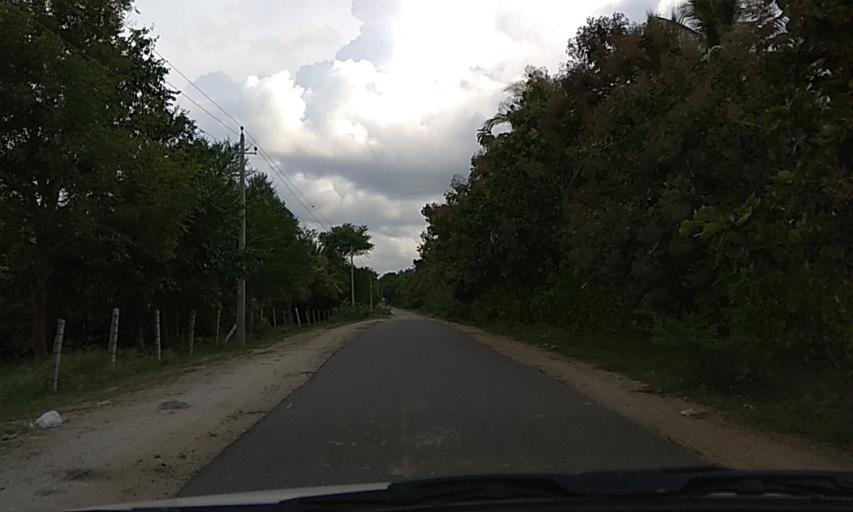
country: IN
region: Karnataka
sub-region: Chamrajnagar
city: Gundlupet
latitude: 11.8825
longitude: 76.7473
